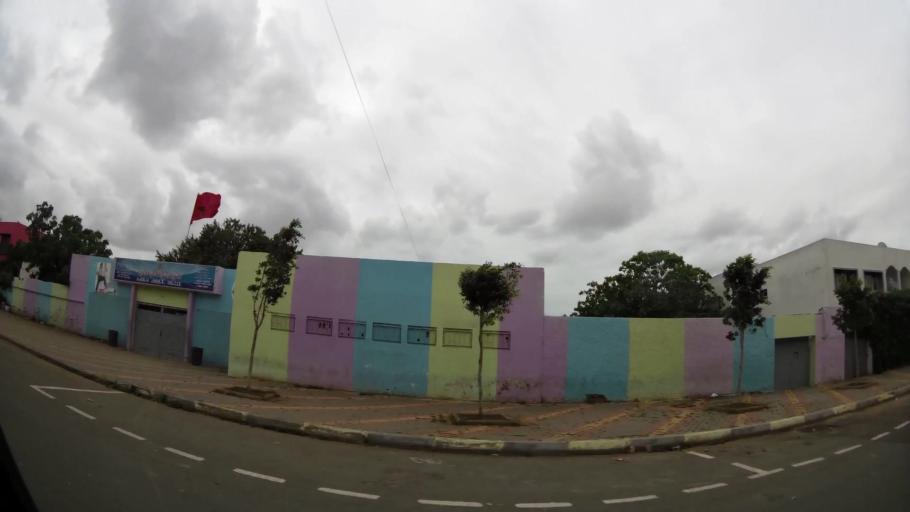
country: MA
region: Grand Casablanca
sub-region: Casablanca
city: Casablanca
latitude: 33.5695
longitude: -7.5688
